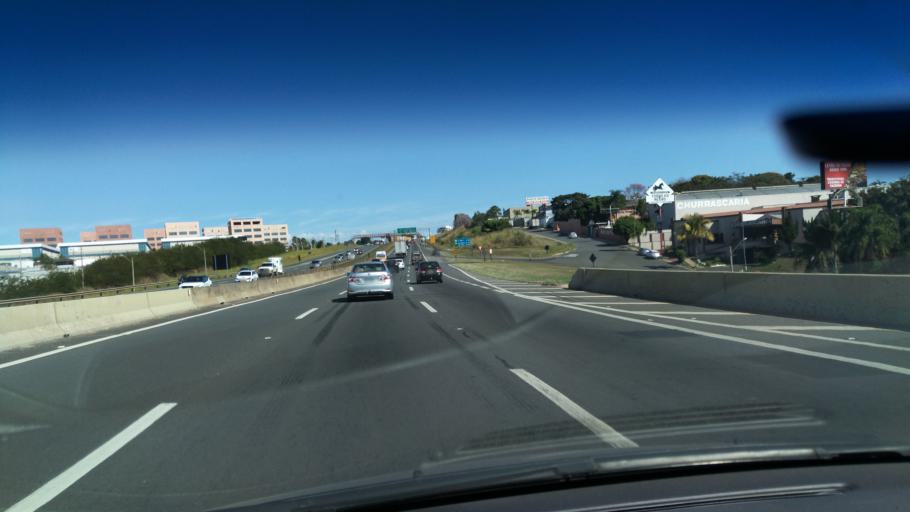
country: BR
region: Sao Paulo
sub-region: Campinas
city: Campinas
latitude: -22.8346
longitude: -47.0335
